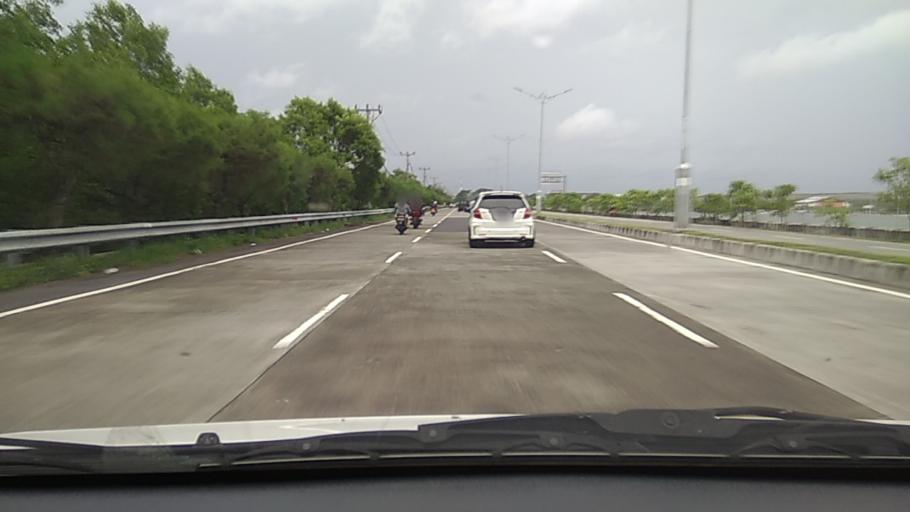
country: ID
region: Bali
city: Karyadharma
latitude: -8.7303
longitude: 115.2126
